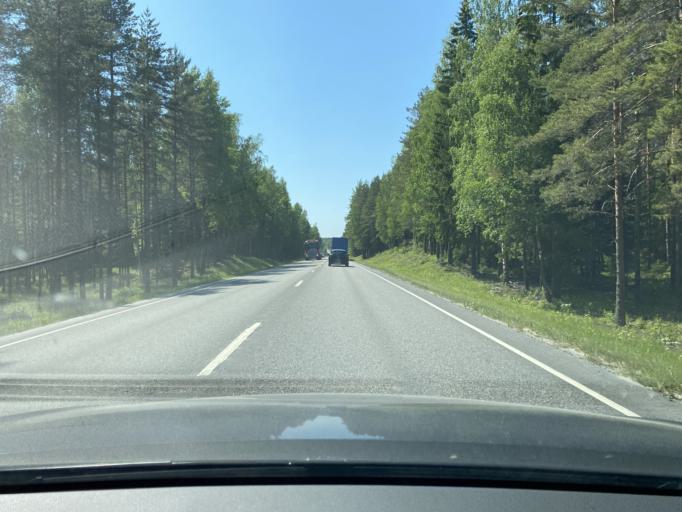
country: FI
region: Pirkanmaa
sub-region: Lounais-Pirkanmaa
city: Mouhijaervi
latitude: 61.3863
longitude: 23.1973
